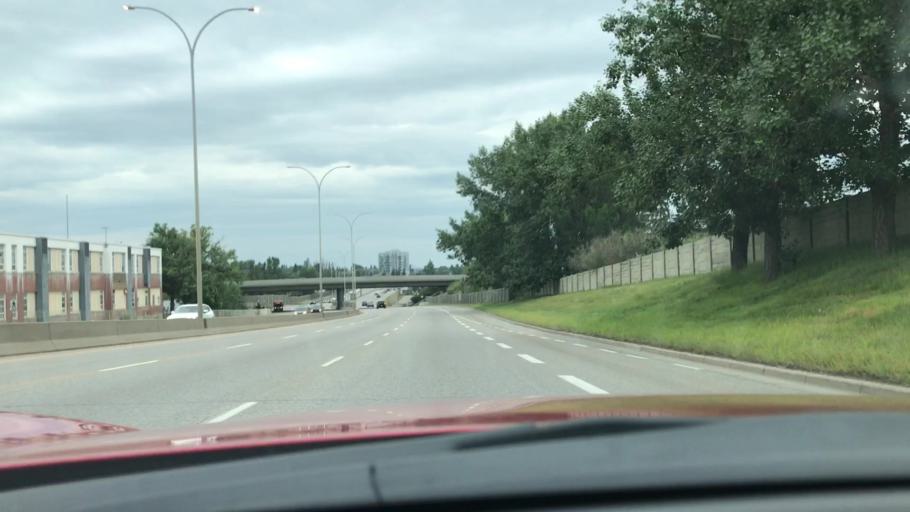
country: CA
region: Alberta
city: Calgary
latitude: 51.0281
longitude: -114.1177
